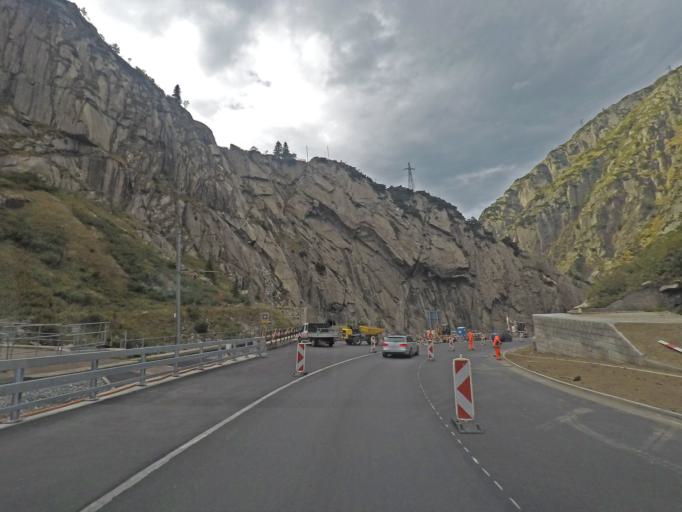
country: CH
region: Uri
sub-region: Uri
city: Andermatt
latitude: 46.6491
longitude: 8.5904
